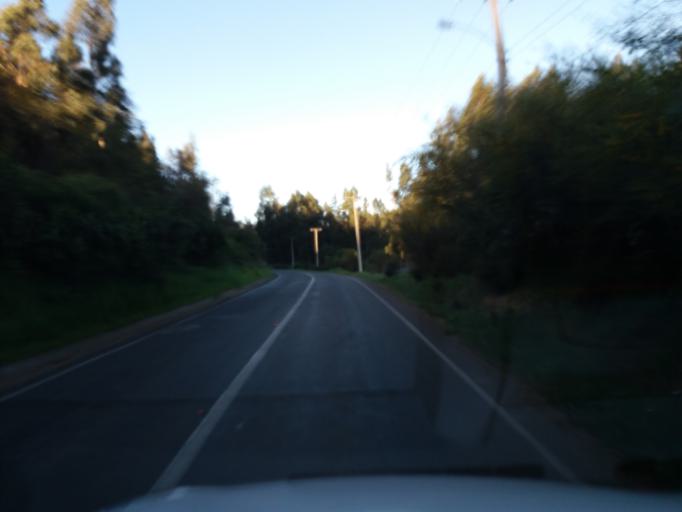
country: CL
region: Valparaiso
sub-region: Provincia de Quillota
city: Quillota
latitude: -32.8868
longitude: -71.2811
